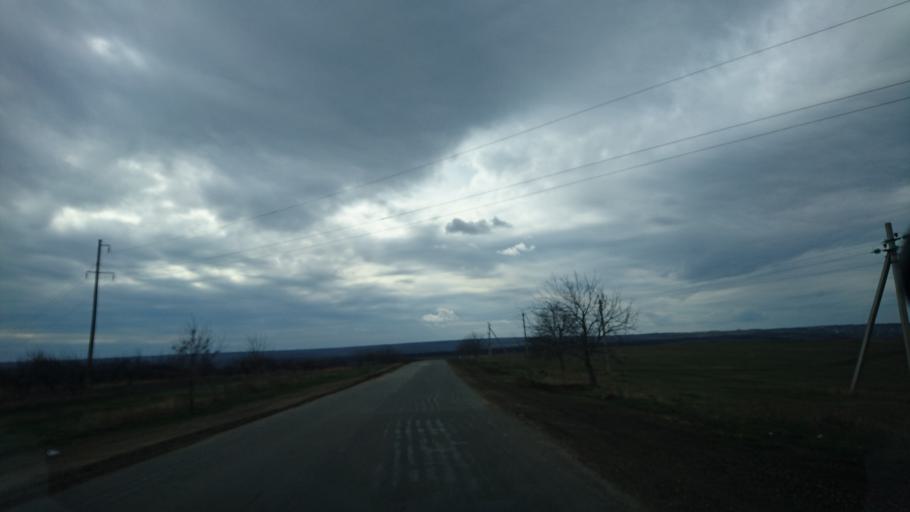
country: MD
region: Cantemir
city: Visniovca
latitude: 46.3293
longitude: 28.4663
